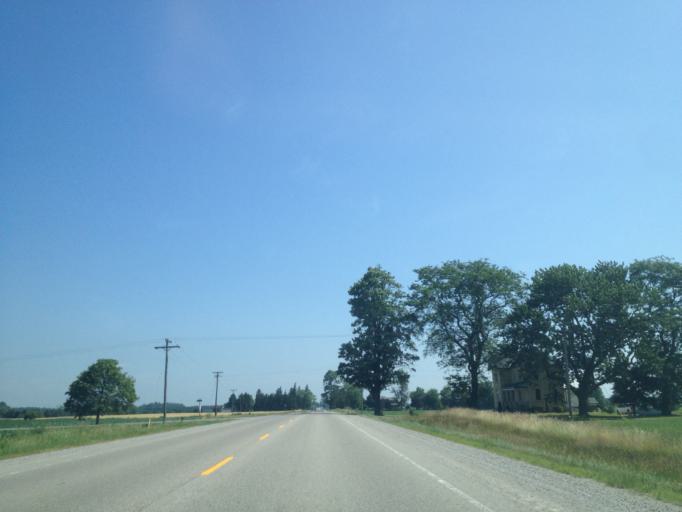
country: CA
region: Ontario
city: London
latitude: 43.2387
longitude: -81.2216
